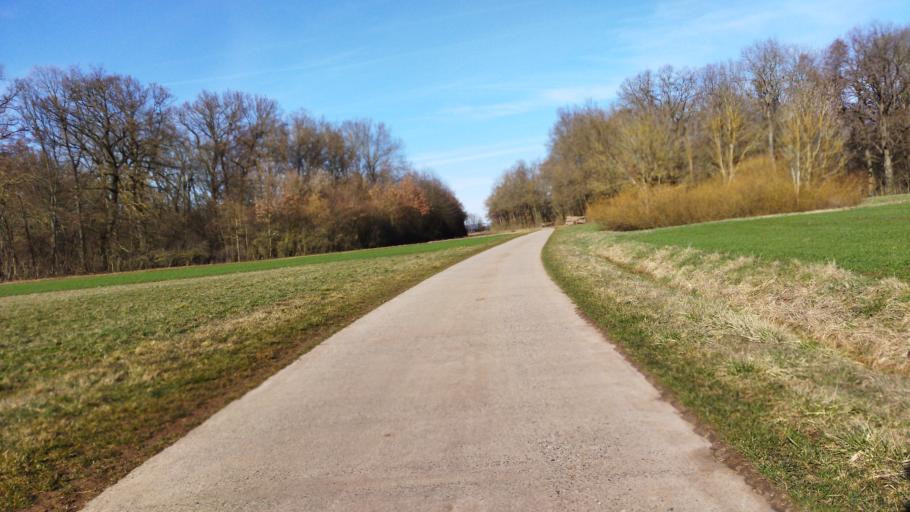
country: DE
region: Bavaria
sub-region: Regierungsbezirk Unterfranken
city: Rothlein
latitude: 49.9802
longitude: 10.1980
